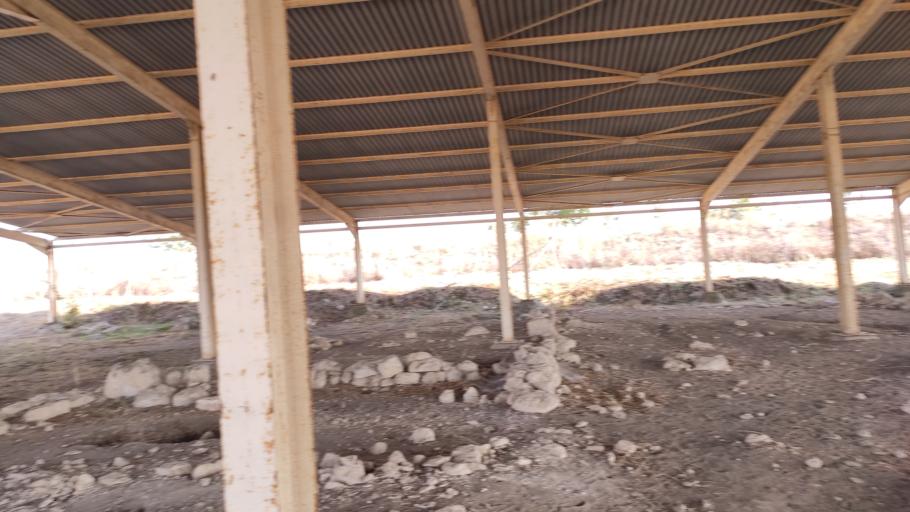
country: GR
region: Central Macedonia
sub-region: Nomos Pellis
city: Pella
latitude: 40.7576
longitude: 22.5191
